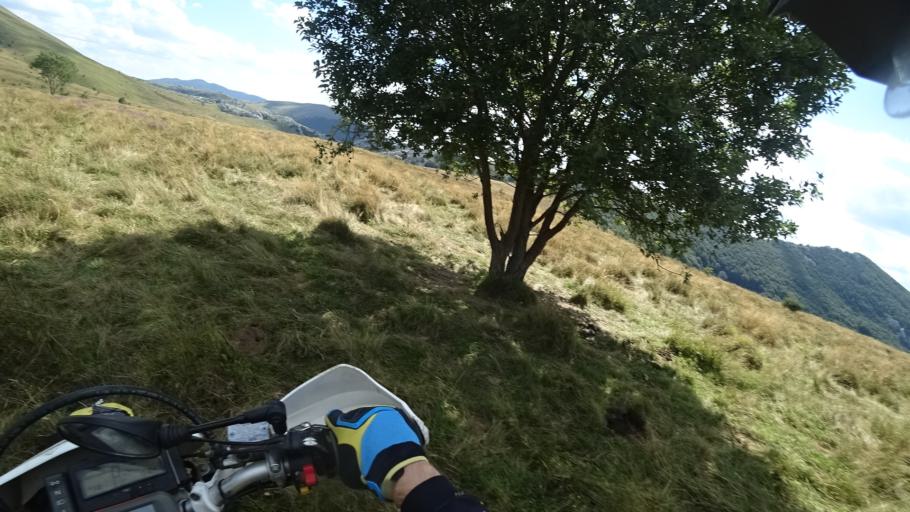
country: HR
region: Zadarska
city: Gracac
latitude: 44.4182
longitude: 15.9995
